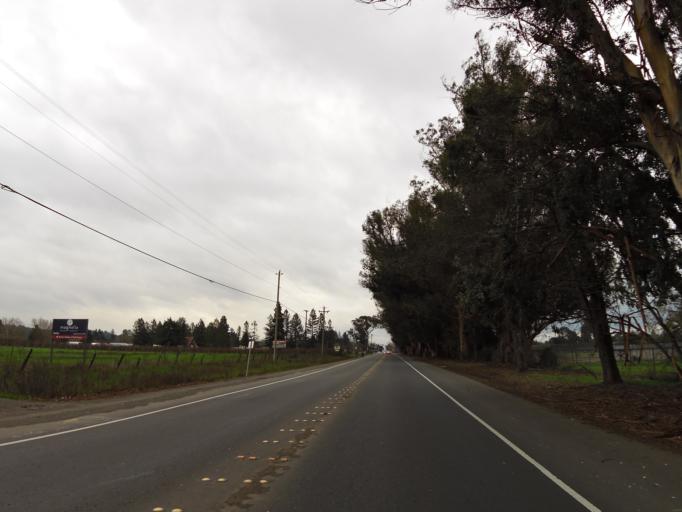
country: US
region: California
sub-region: Sonoma County
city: Rohnert Park
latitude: 38.3399
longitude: -122.6669
